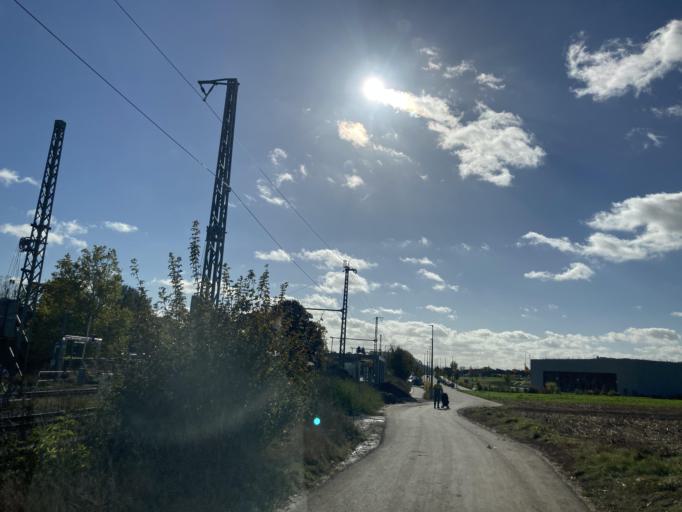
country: DE
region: Baden-Wuerttemberg
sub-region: Regierungsbezirk Stuttgart
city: Hildrizhausen
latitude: 48.5531
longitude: 8.9625
